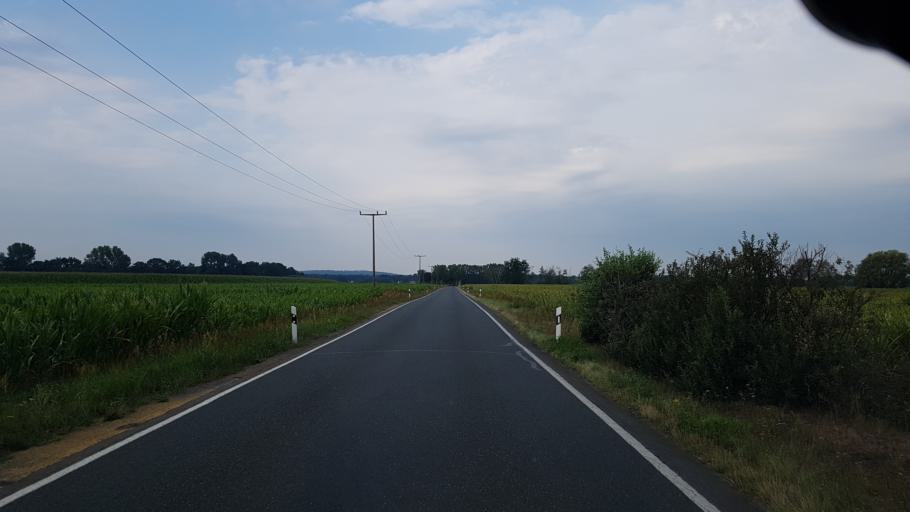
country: DE
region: Brandenburg
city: Tettau
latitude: 51.4172
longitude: 13.7268
